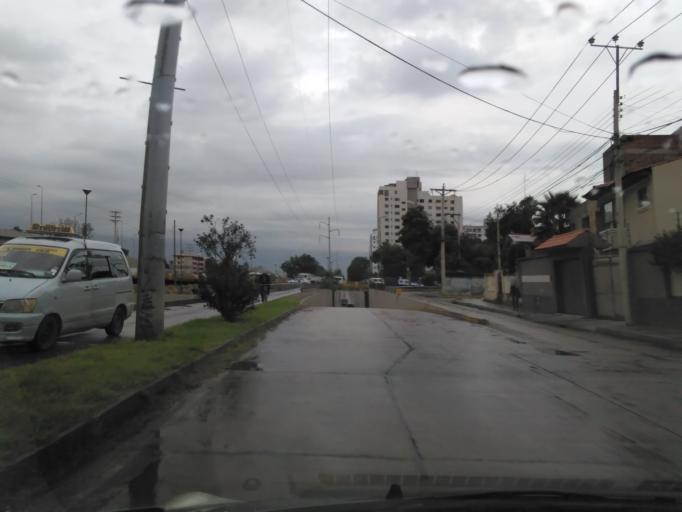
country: BO
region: Cochabamba
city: Cochabamba
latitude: -17.3765
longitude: -66.1414
